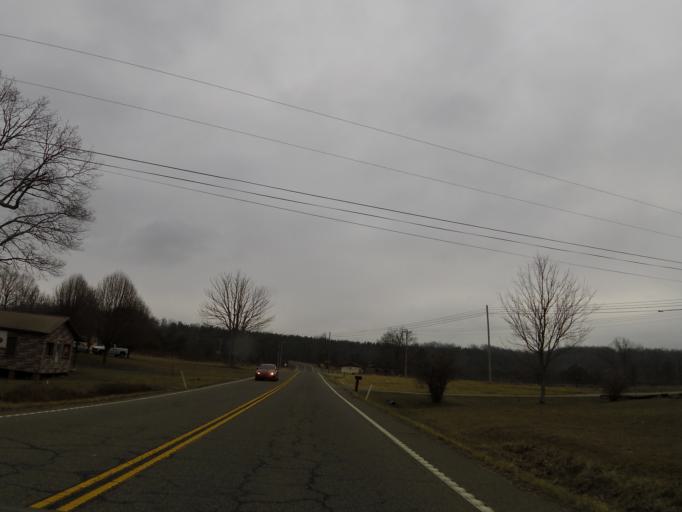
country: US
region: Tennessee
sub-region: Morgan County
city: Wartburg
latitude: 36.2899
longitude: -84.6570
